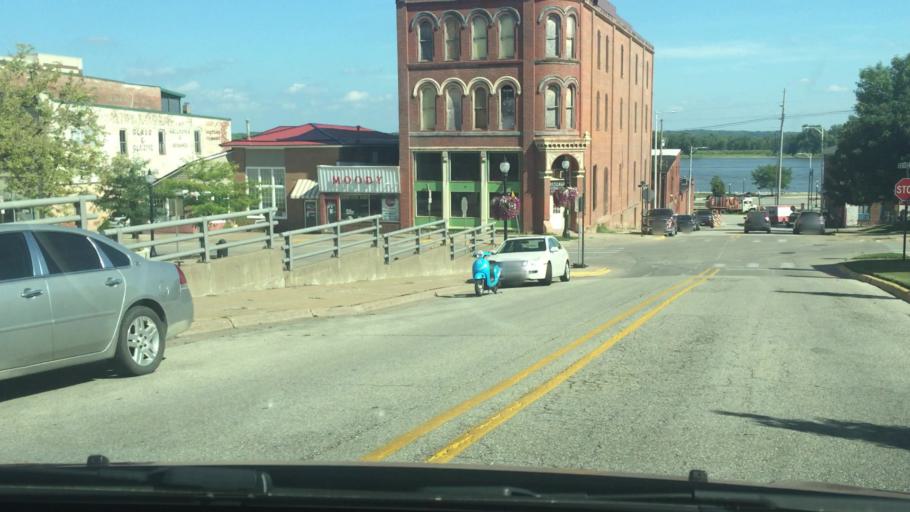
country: US
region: Iowa
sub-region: Muscatine County
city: Muscatine
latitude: 41.4204
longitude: -91.0482
